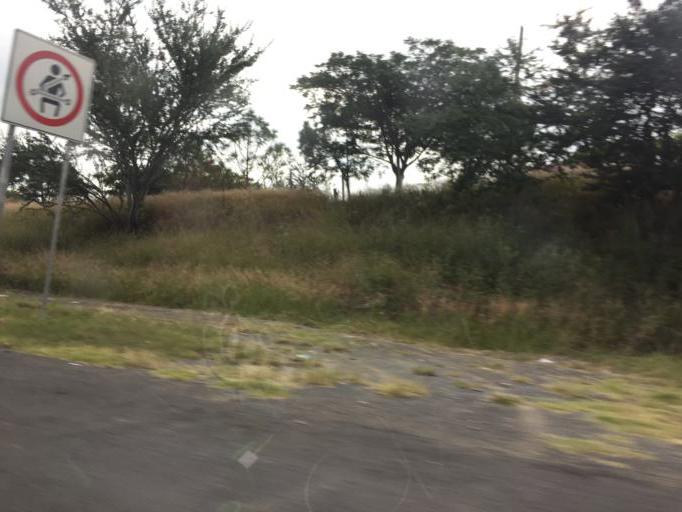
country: MX
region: Jalisco
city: Ocotlan
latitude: 20.4012
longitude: -102.7344
